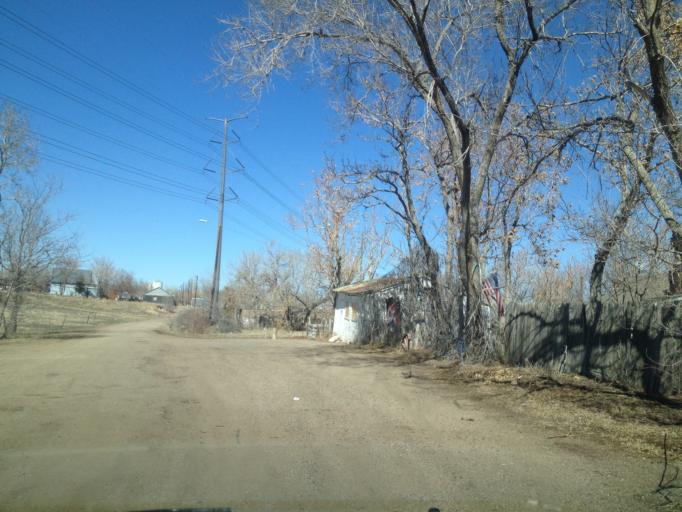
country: US
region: Colorado
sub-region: Adams County
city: Twin Lakes
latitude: 39.7858
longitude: -104.9836
